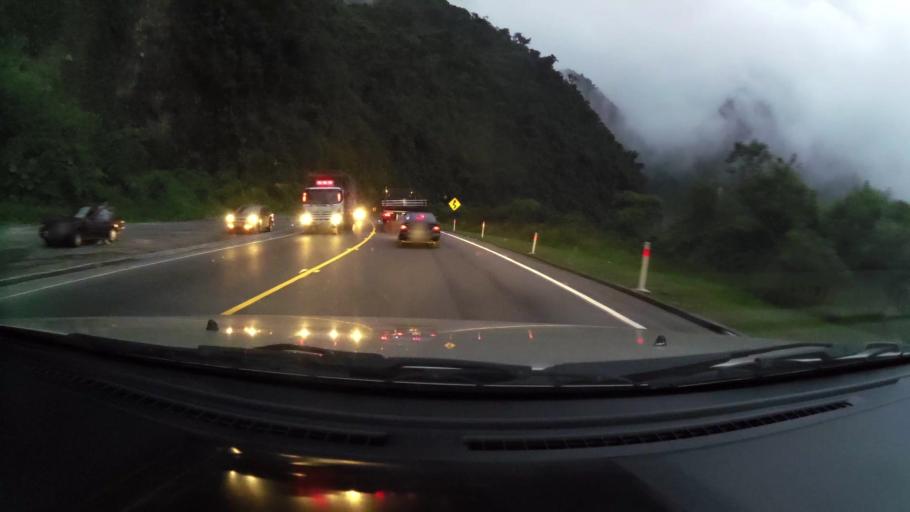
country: EC
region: Pichincha
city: Machachi
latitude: -0.4514
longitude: -78.6842
